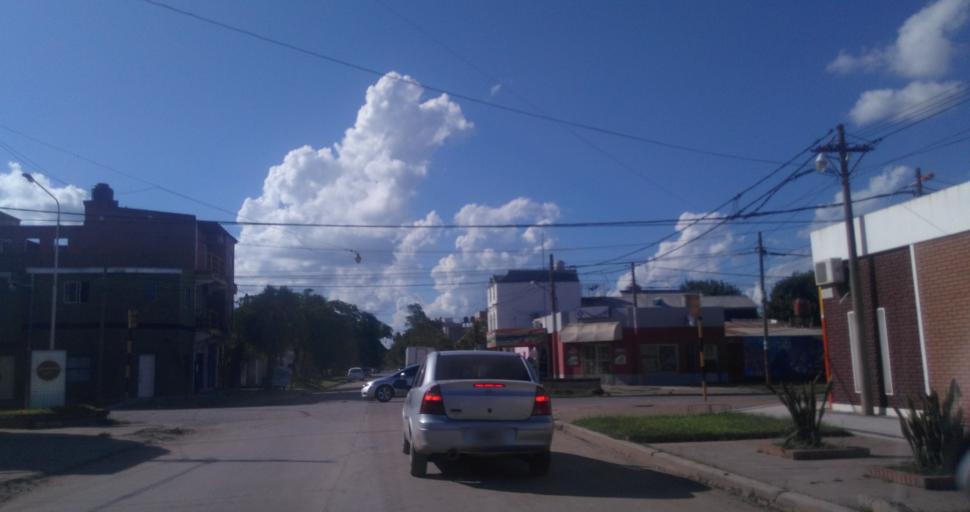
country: AR
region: Chaco
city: Resistencia
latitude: -27.4672
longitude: -58.9754
